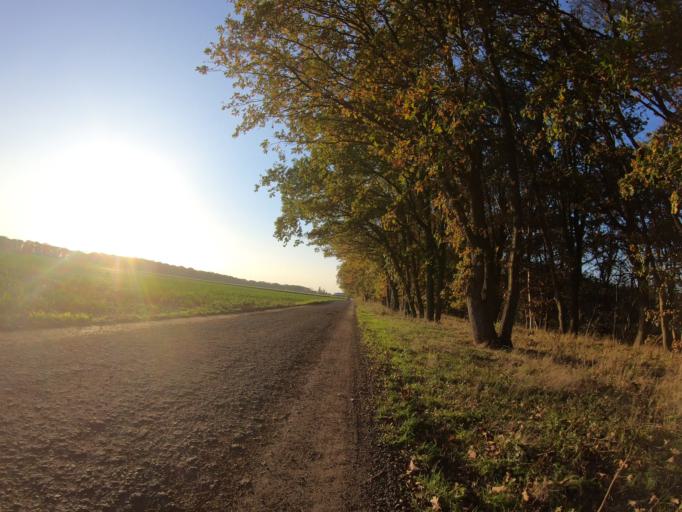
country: DE
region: Lower Saxony
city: Wagenhoff
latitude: 52.5128
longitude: 10.4981
